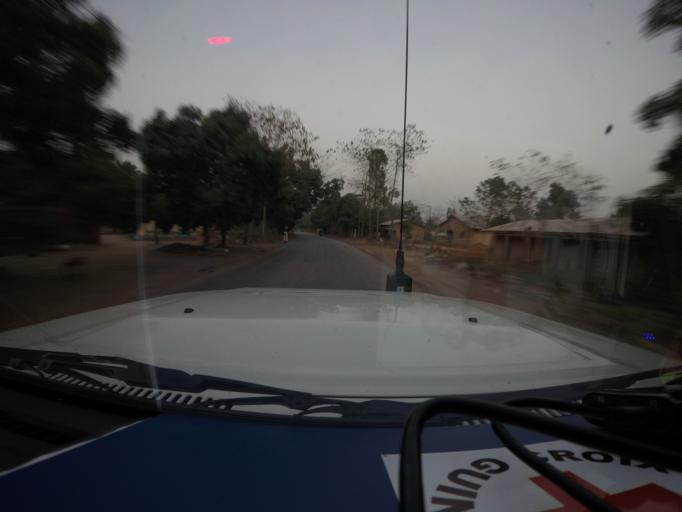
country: GN
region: Kindia
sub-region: Kindia
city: Kindia
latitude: 9.9342
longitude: -12.9836
